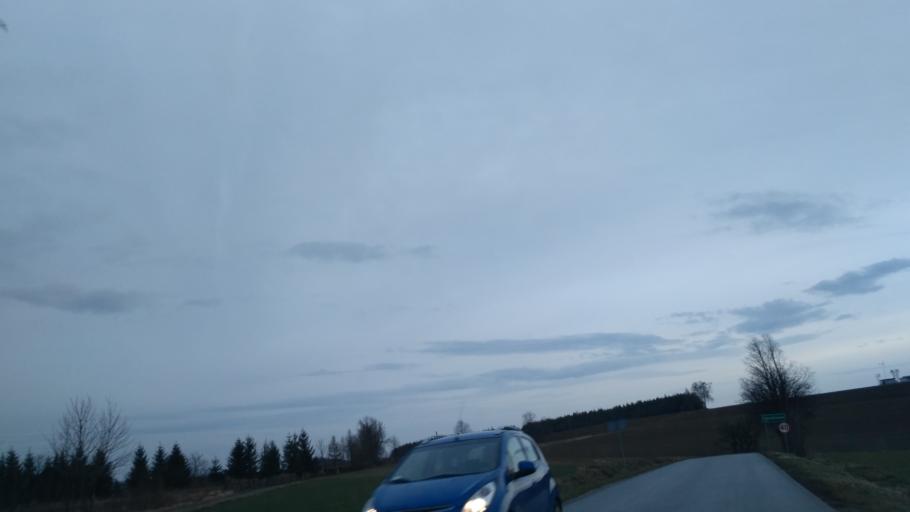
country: PL
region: Subcarpathian Voivodeship
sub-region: Powiat strzyzowski
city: Polomia
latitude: 49.8751
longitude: 21.8581
